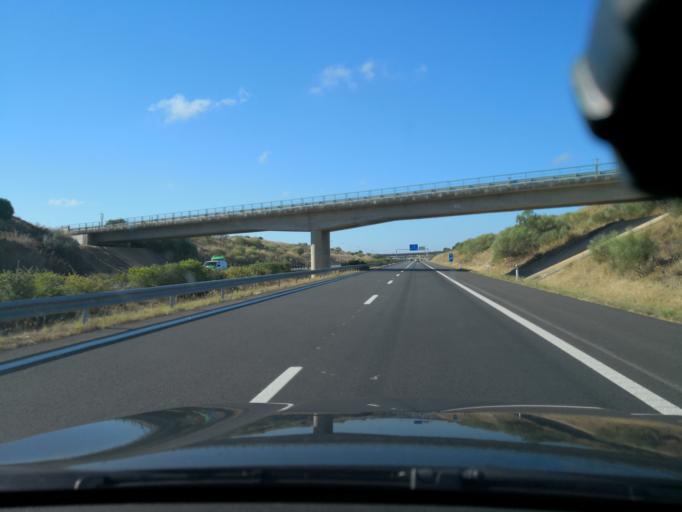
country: PT
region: Beja
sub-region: Aljustrel
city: Aljustrel
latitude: 37.8980
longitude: -8.2407
